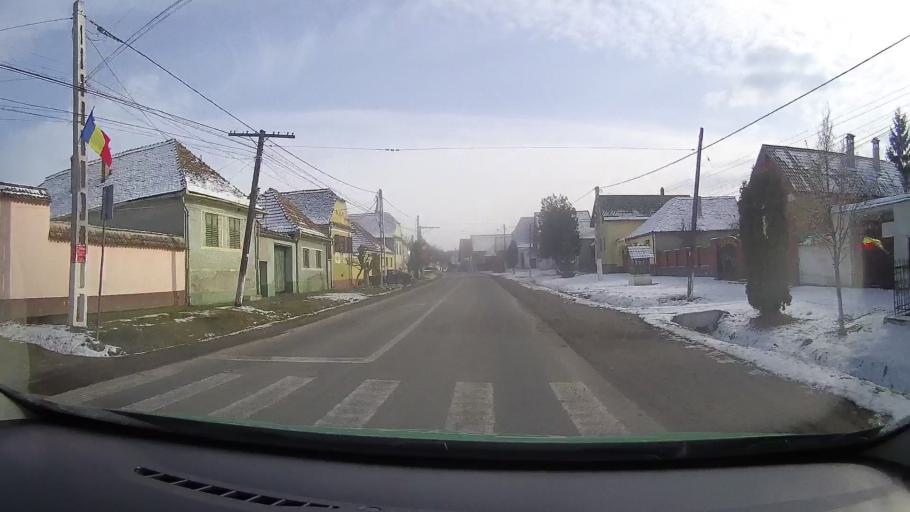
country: RO
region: Mures
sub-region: Comuna Apold
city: Saes
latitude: 46.1578
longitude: 24.7667
